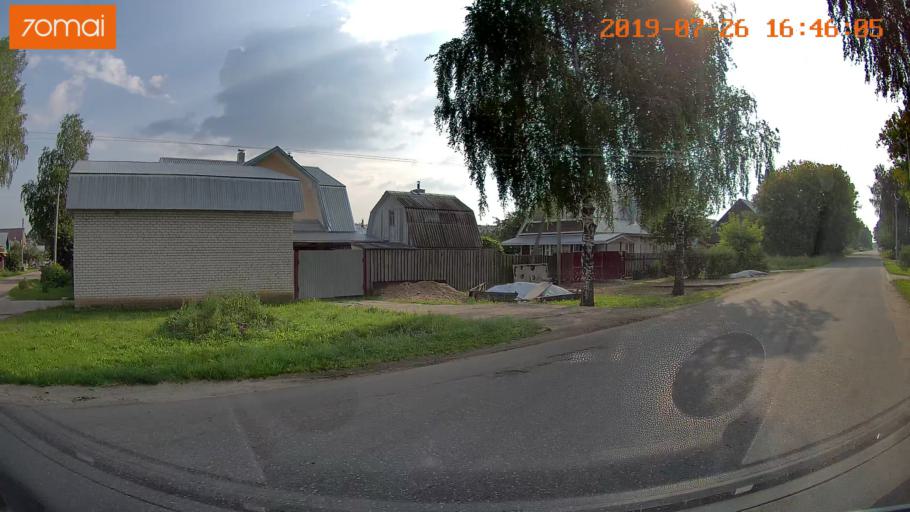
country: RU
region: Ivanovo
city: Bogorodskoye
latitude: 57.0448
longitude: 41.0221
